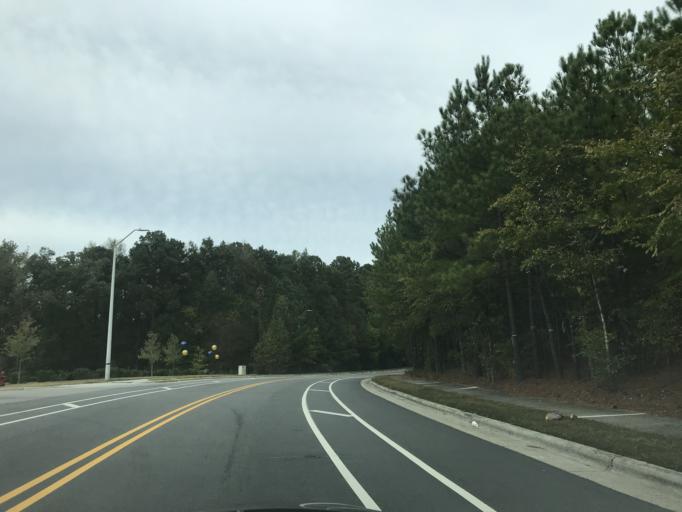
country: US
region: North Carolina
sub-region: Wake County
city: Wake Forest
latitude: 35.9471
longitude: -78.5483
